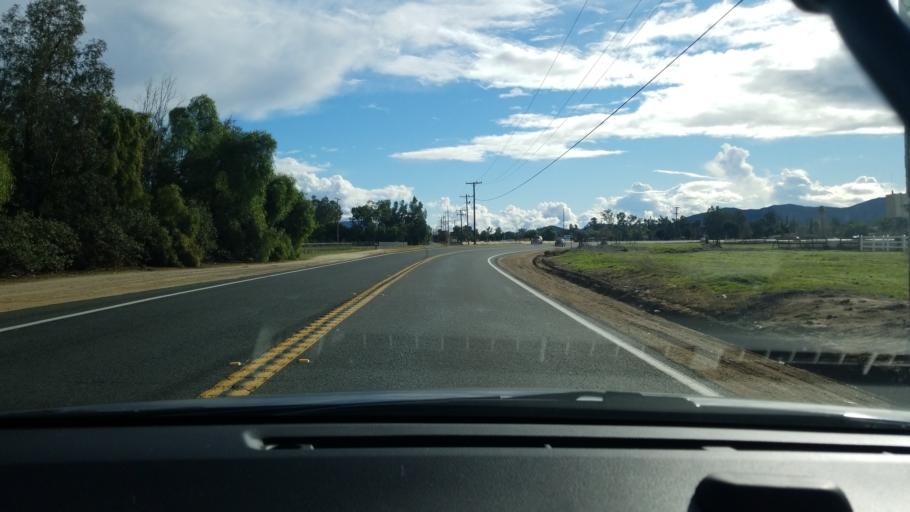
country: US
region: California
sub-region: Riverside County
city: Winchester
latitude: 33.7179
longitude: -117.0764
